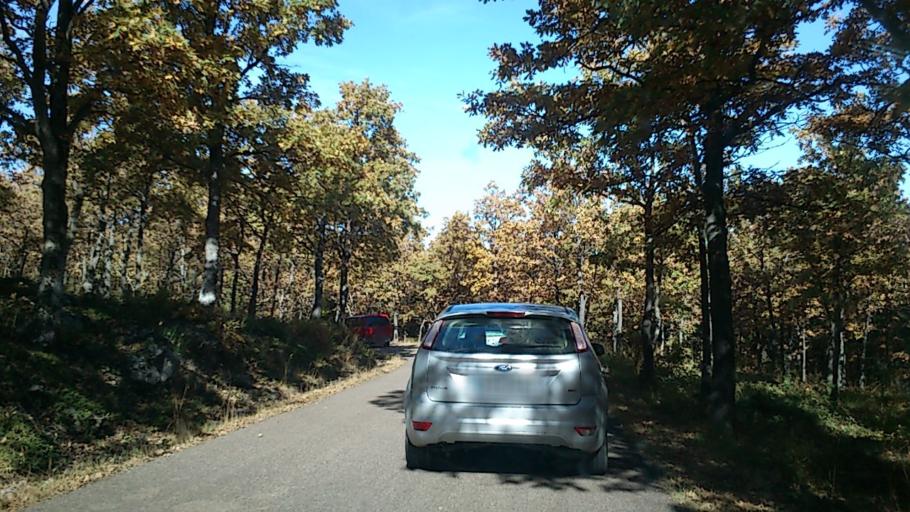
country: ES
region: Aragon
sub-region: Provincia de Zaragoza
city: Lituenigo
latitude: 41.8083
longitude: -1.8017
